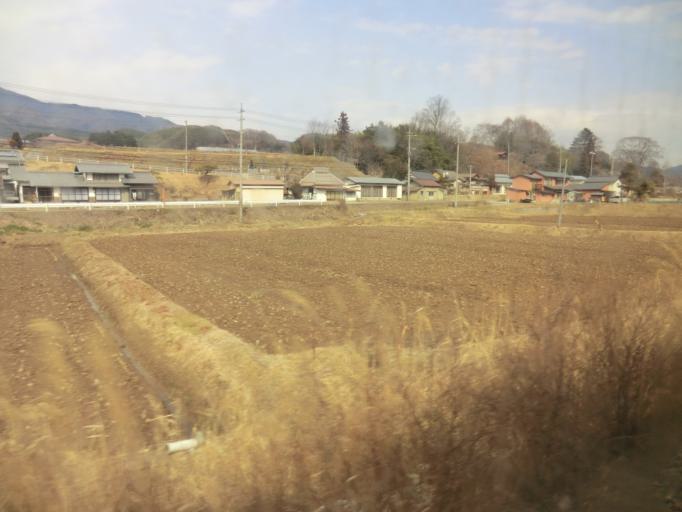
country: JP
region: Nagano
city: Omachi
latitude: 36.4456
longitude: 138.0308
